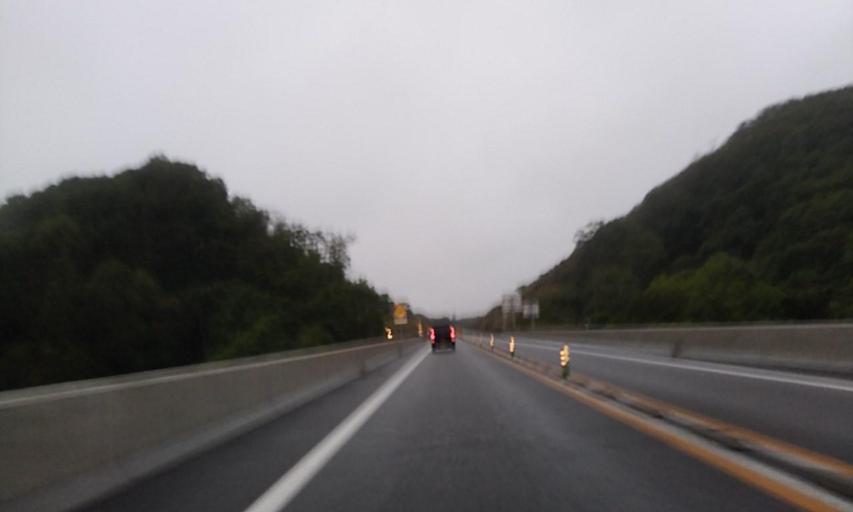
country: JP
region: Hokkaido
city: Kushiro
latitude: 43.0037
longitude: 144.4999
